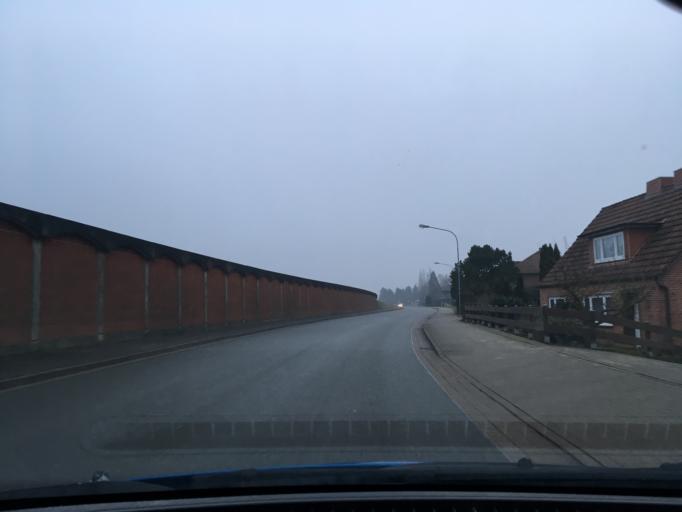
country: DE
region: Lower Saxony
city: Stelle
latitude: 53.4320
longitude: 10.0995
